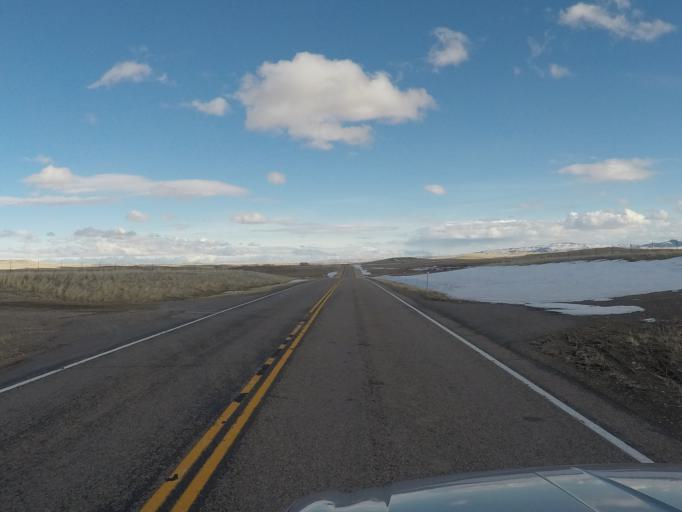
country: US
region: Montana
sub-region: Meagher County
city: White Sulphur Springs
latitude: 46.5038
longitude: -110.3711
